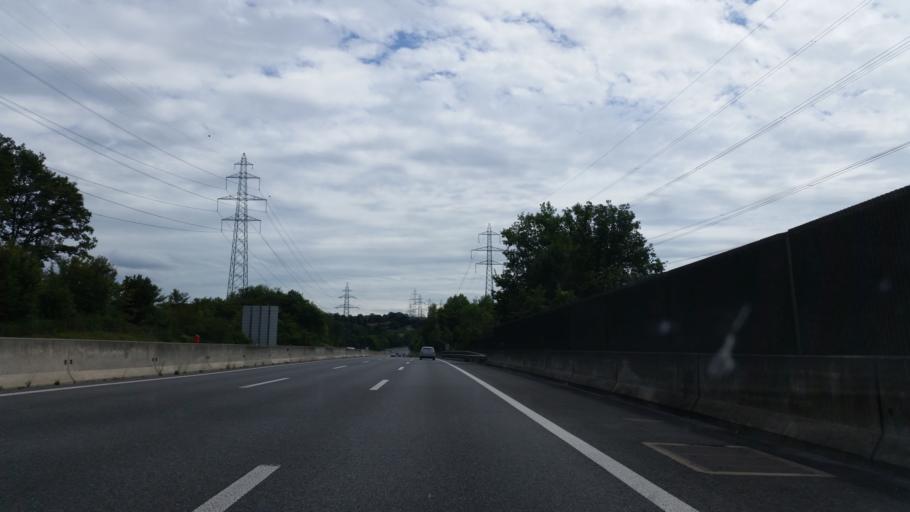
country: CH
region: Vaud
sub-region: Ouest Lausannois District
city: Crissier
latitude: 46.5619
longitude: 6.5825
